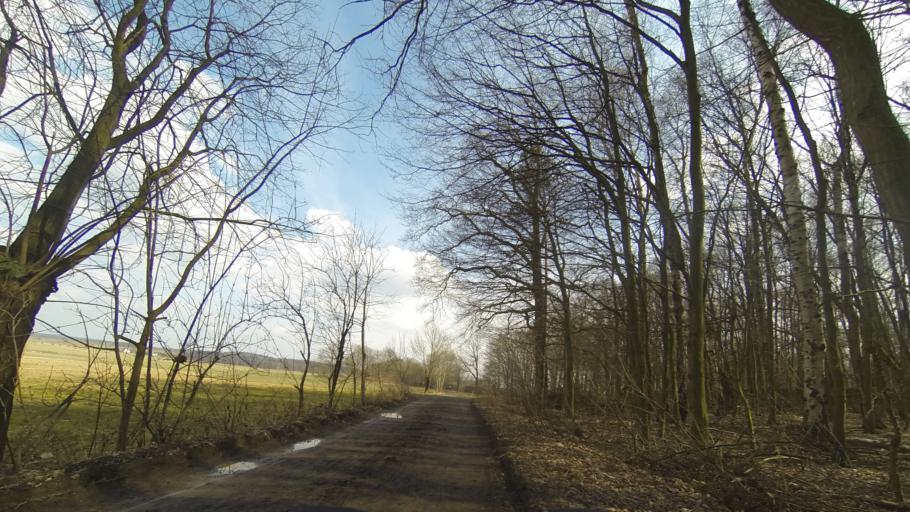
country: DE
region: Saxony
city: Moritzburg
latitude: 51.1732
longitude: 13.7042
